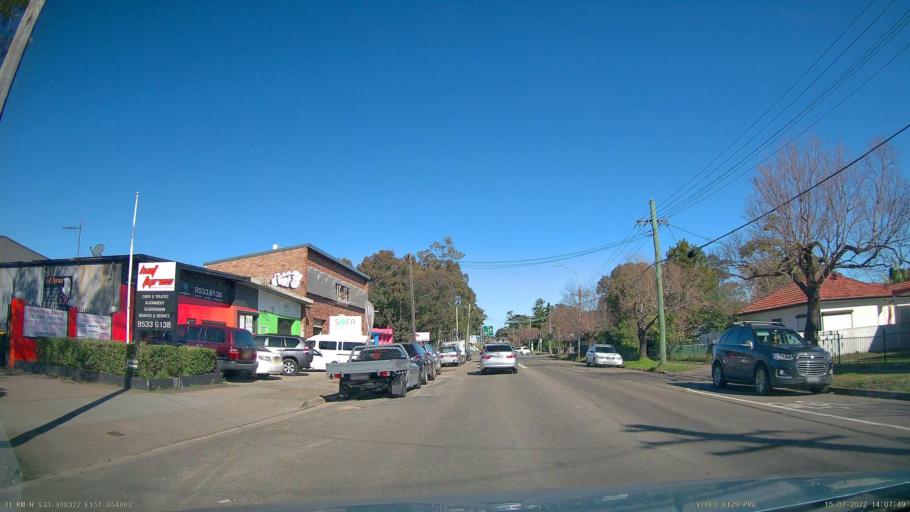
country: AU
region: New South Wales
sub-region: Canterbury
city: Roselands
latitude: -33.9384
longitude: 151.0549
